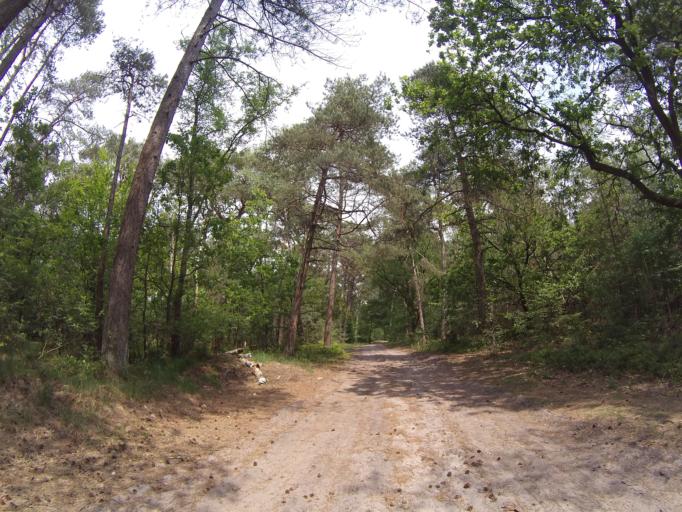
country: NL
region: Utrecht
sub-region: Gemeente Utrechtse Heuvelrug
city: Driebergen-Rijsenburg
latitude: 52.0964
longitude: 5.3178
